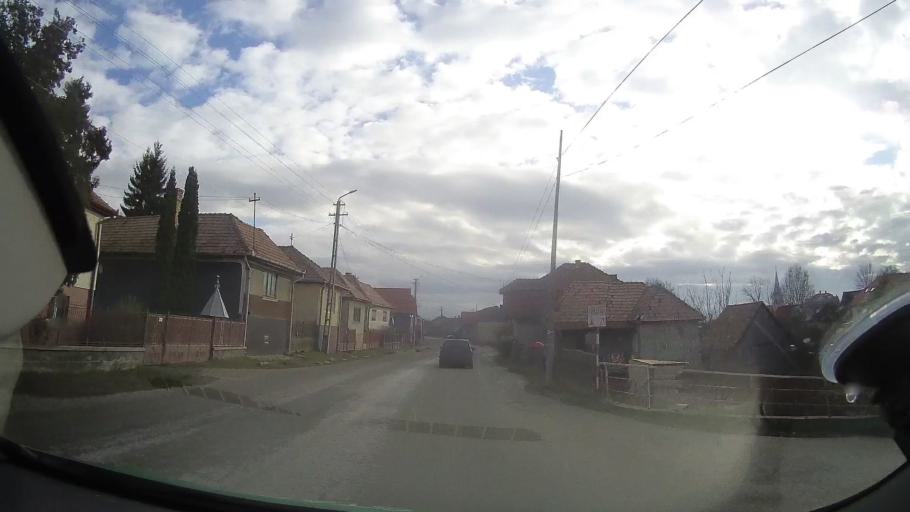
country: RO
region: Cluj
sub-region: Comuna Baisoara
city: Baisoara
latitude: 46.6182
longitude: 23.4564
